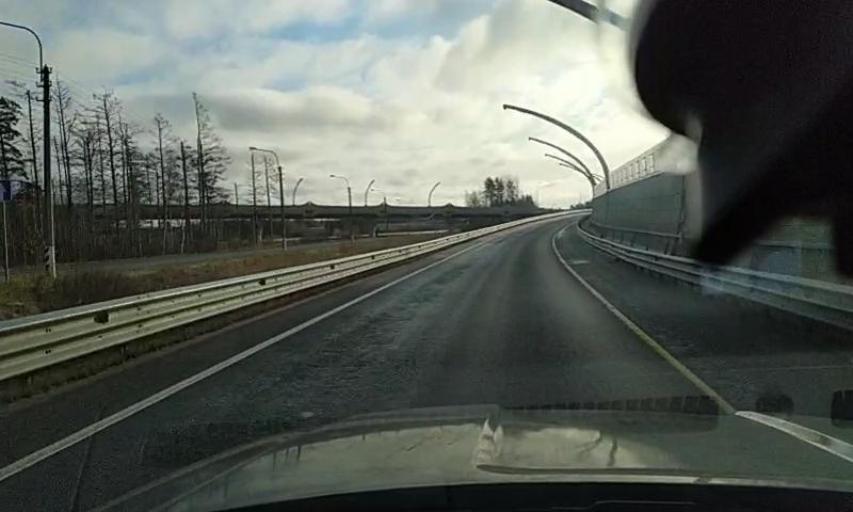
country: RU
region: St.-Petersburg
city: Solnechnoye
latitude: 60.1521
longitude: 29.9699
